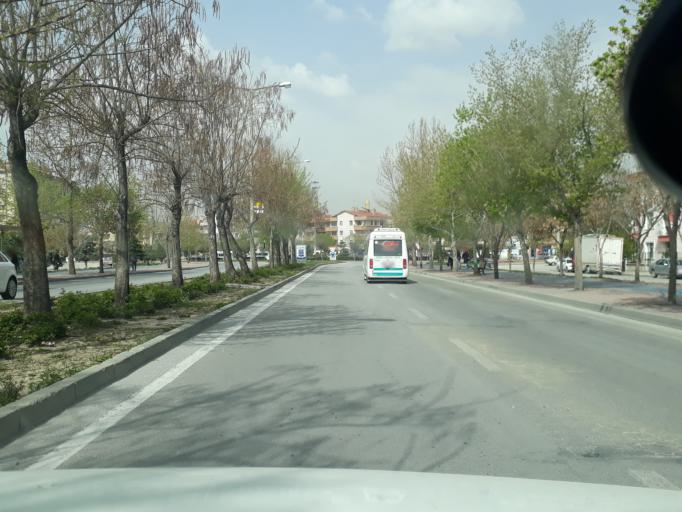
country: TR
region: Konya
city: Selcuklu
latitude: 37.9372
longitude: 32.4948
